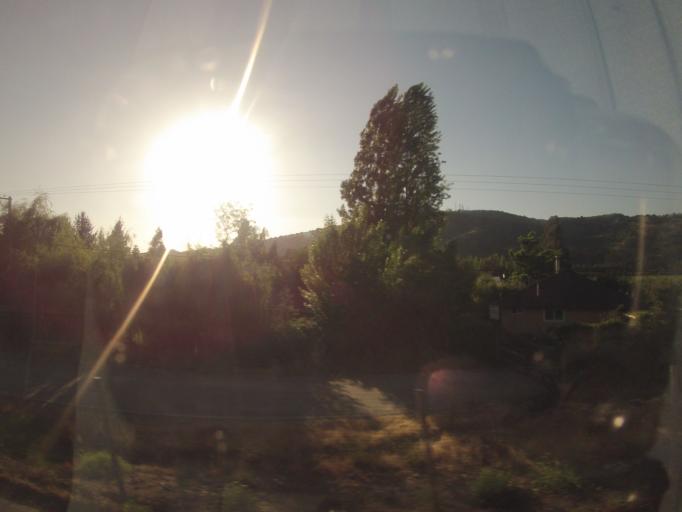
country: CL
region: O'Higgins
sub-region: Provincia de Colchagua
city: Chimbarongo
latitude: -34.6388
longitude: -70.9909
